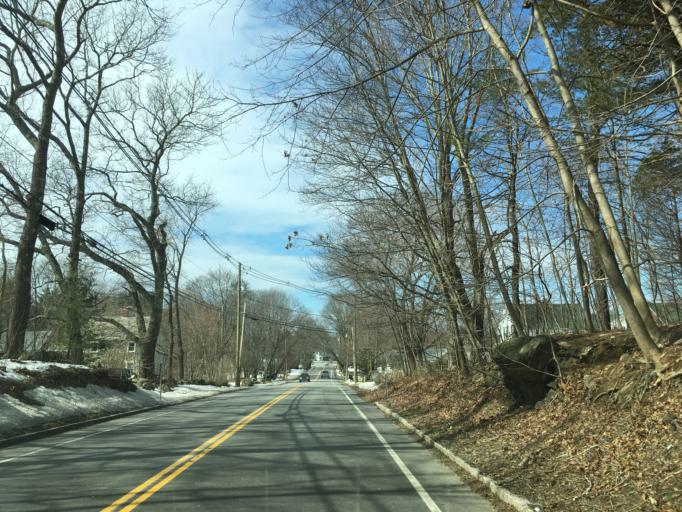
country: US
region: New Hampshire
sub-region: Rockingham County
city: North Hampton
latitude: 42.9765
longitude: -70.8405
